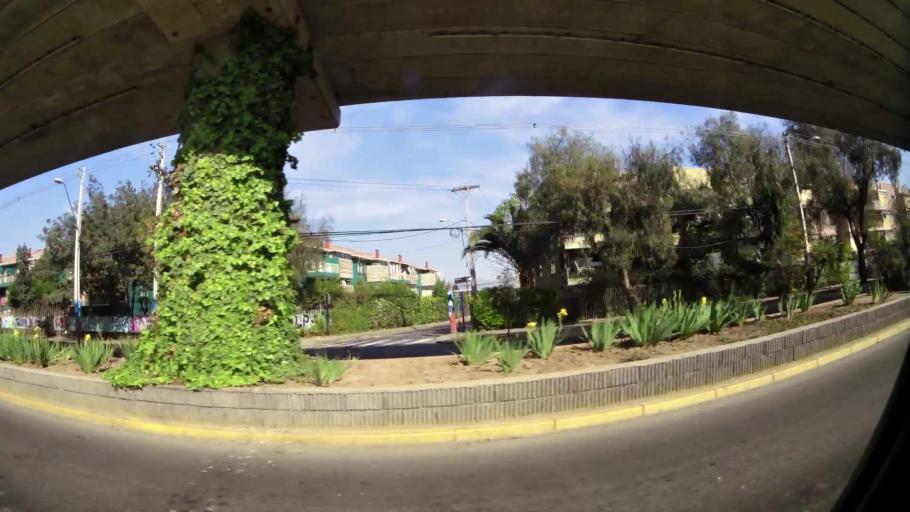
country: CL
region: Santiago Metropolitan
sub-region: Provincia de Santiago
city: Lo Prado
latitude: -33.4638
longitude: -70.7377
